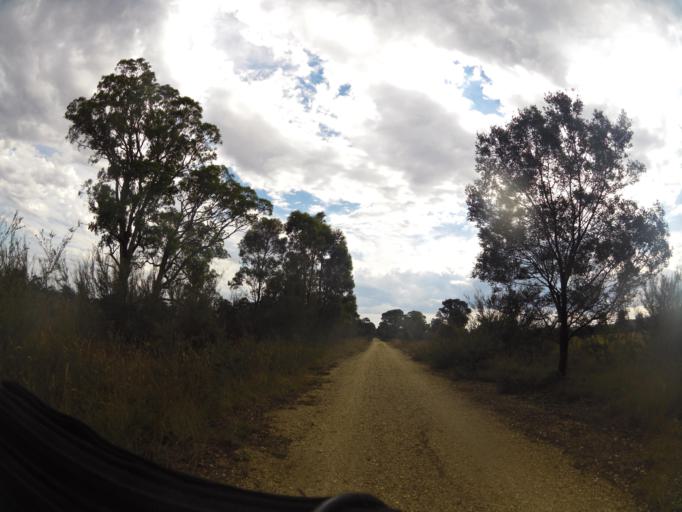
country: AU
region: Victoria
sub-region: Wellington
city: Heyfield
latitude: -38.0428
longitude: 146.6431
